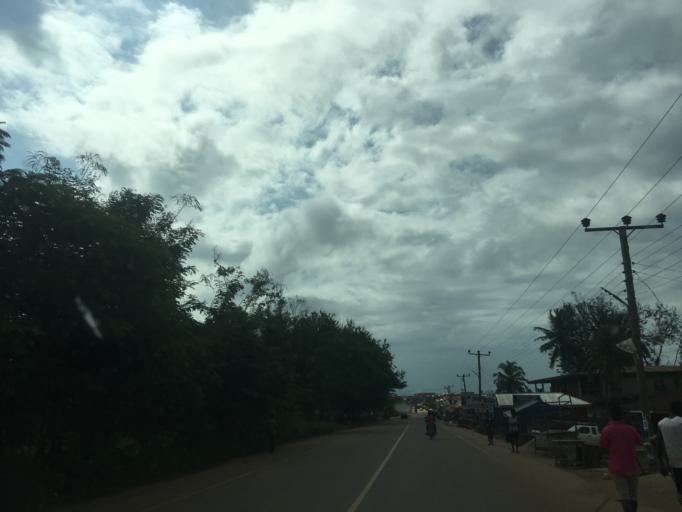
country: GH
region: Western
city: Wassa-Akropong
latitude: 5.8028
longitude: -2.4309
